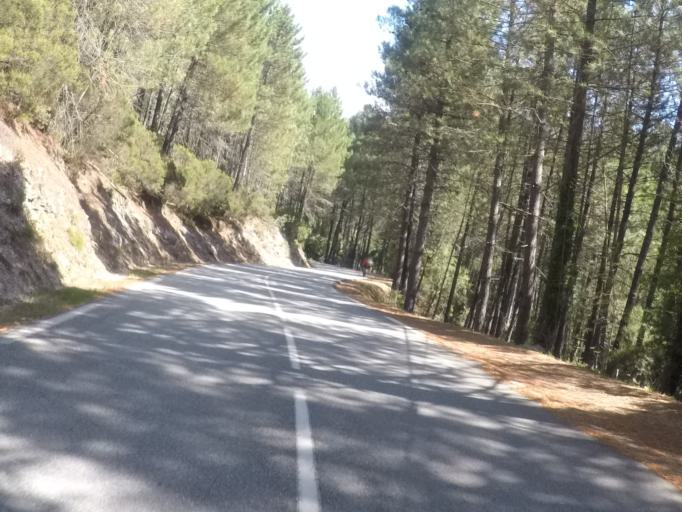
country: FR
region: Corsica
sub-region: Departement de la Corse-du-Sud
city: Zonza
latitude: 41.7654
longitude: 9.2014
